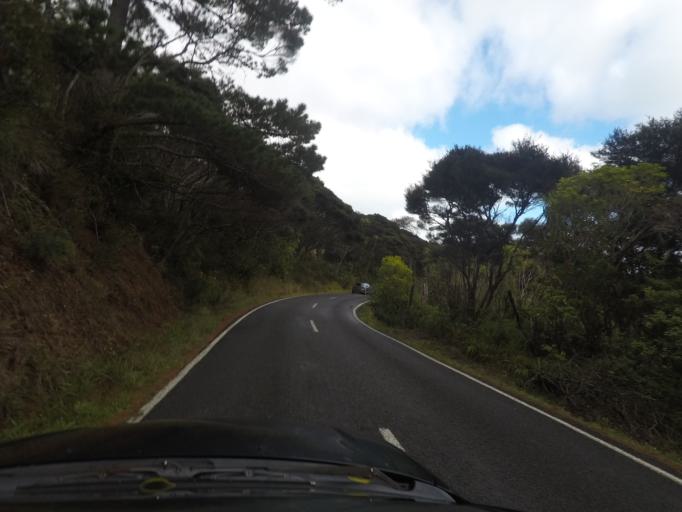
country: NZ
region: Auckland
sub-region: Auckland
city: Muriwai Beach
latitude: -36.8758
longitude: 174.4579
